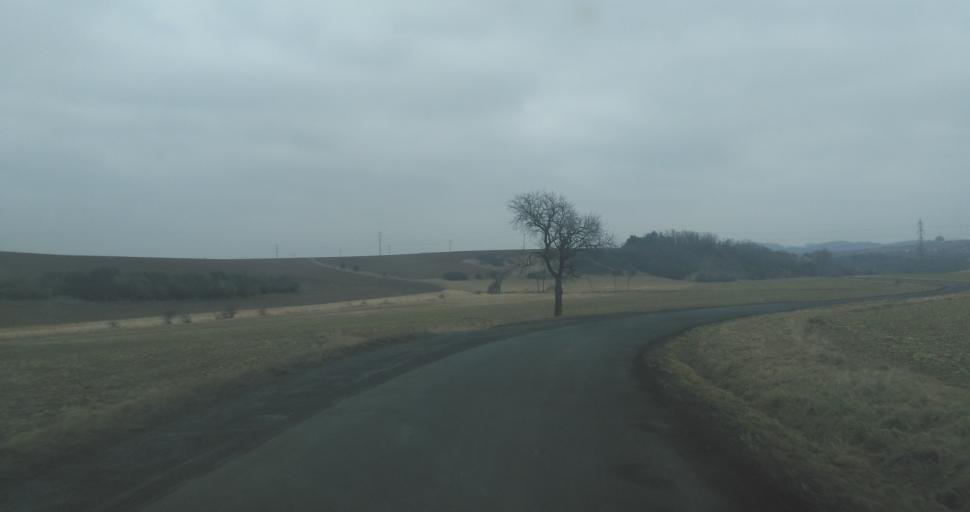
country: CZ
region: Central Bohemia
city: Zebrak
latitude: 49.8830
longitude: 13.9311
